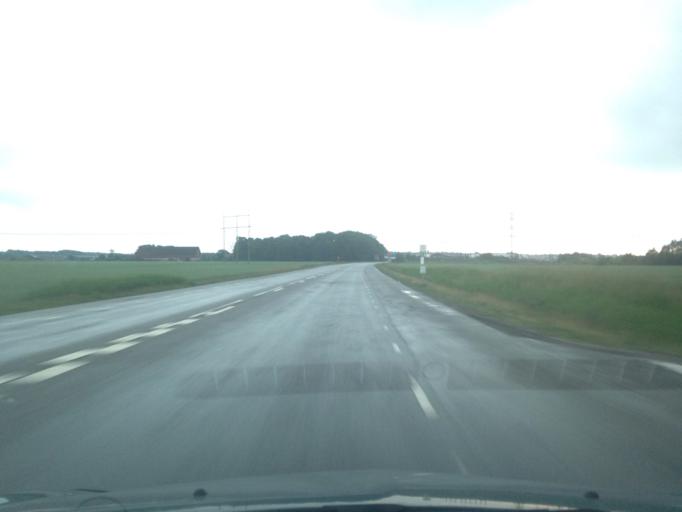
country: SE
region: Halland
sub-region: Varbergs Kommun
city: Varberg
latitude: 57.1274
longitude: 12.3091
